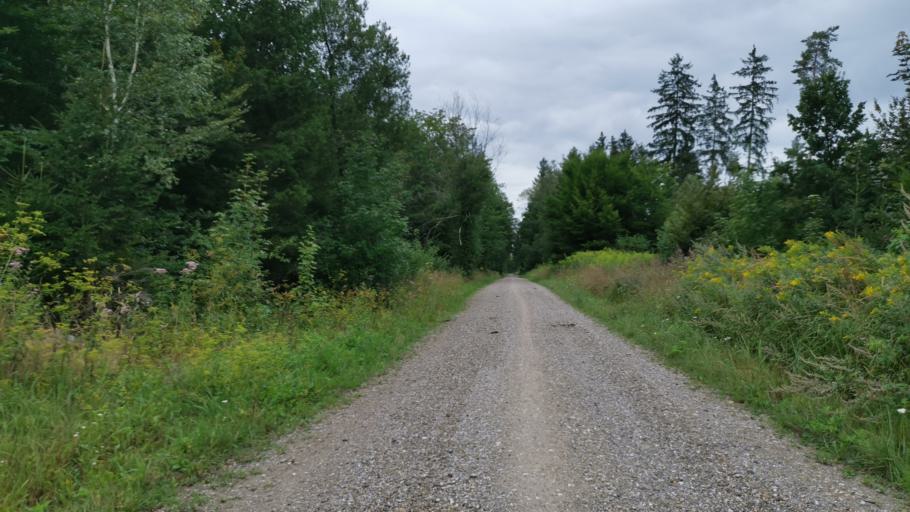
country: DE
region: Bavaria
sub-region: Upper Bavaria
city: Pullach im Isartal
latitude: 48.0718
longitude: 11.5619
